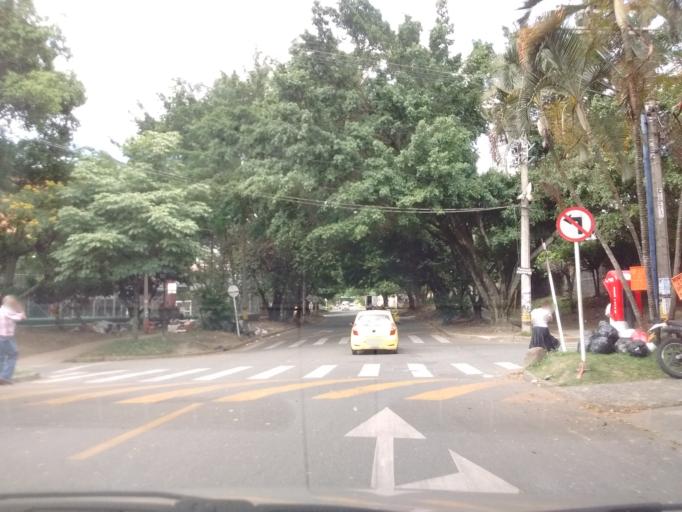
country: CO
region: Antioquia
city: Medellin
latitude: 6.2488
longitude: -75.6051
